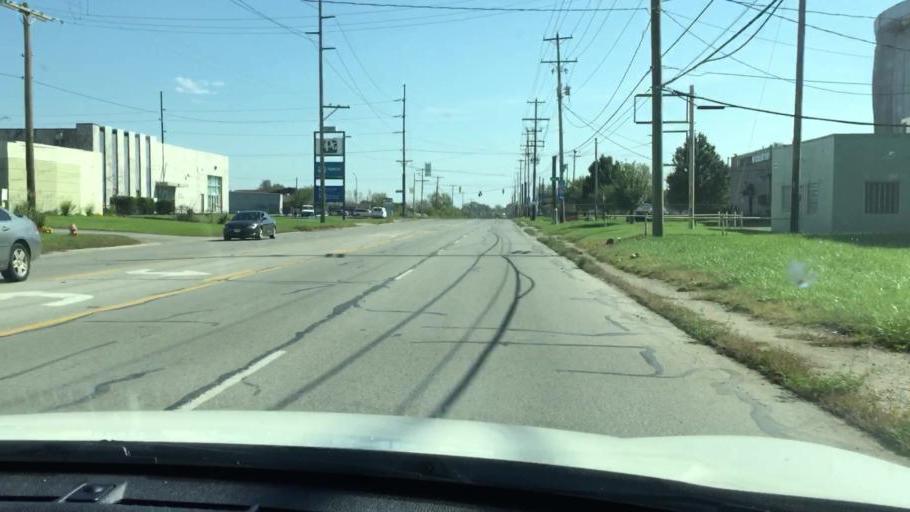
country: US
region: Ohio
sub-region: Franklin County
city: Bexley
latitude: 39.9856
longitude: -82.9689
